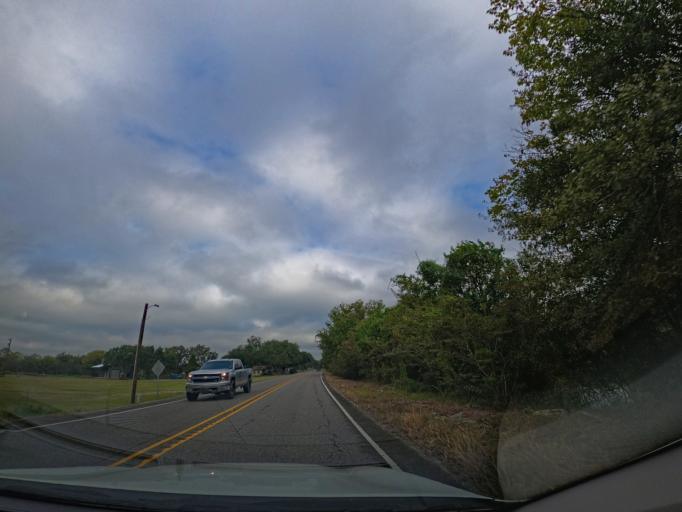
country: US
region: Louisiana
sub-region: Terrebonne Parish
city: Bayou Cane
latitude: 29.5772
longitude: -90.8117
